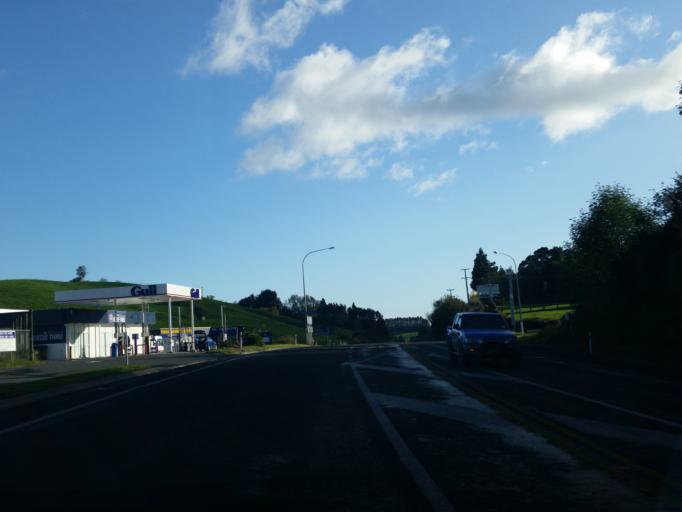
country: NZ
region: Bay of Plenty
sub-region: Tauranga City
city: Tauranga
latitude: -37.6810
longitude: 176.0255
